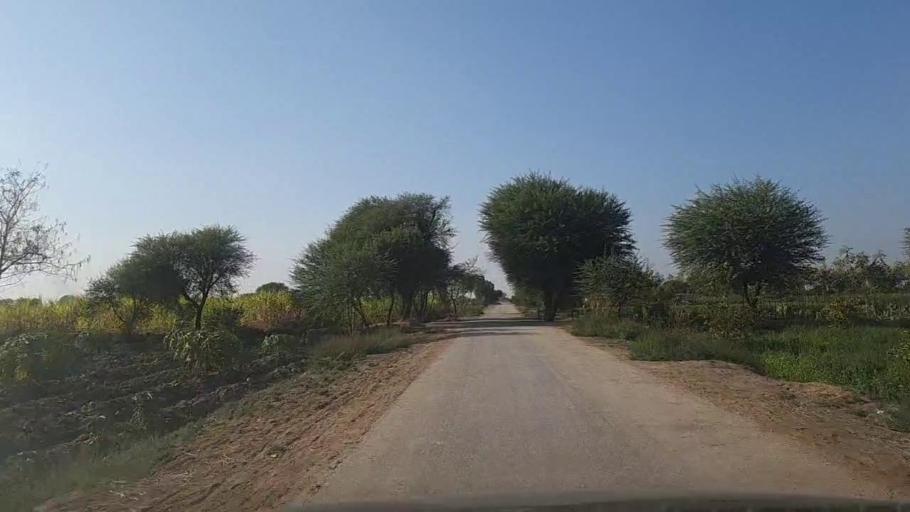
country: PK
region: Sindh
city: Digri
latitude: 25.0250
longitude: 69.2275
